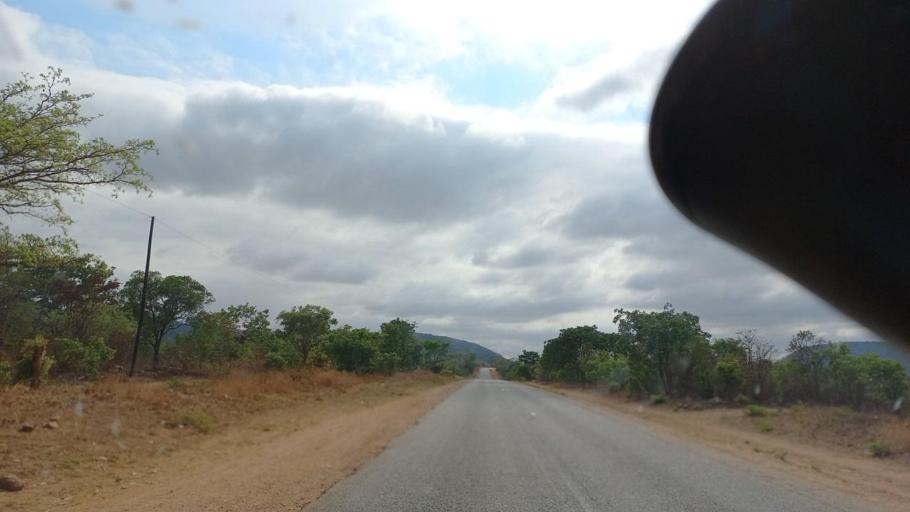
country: ZM
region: Lusaka
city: Chongwe
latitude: -15.1337
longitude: 29.4441
